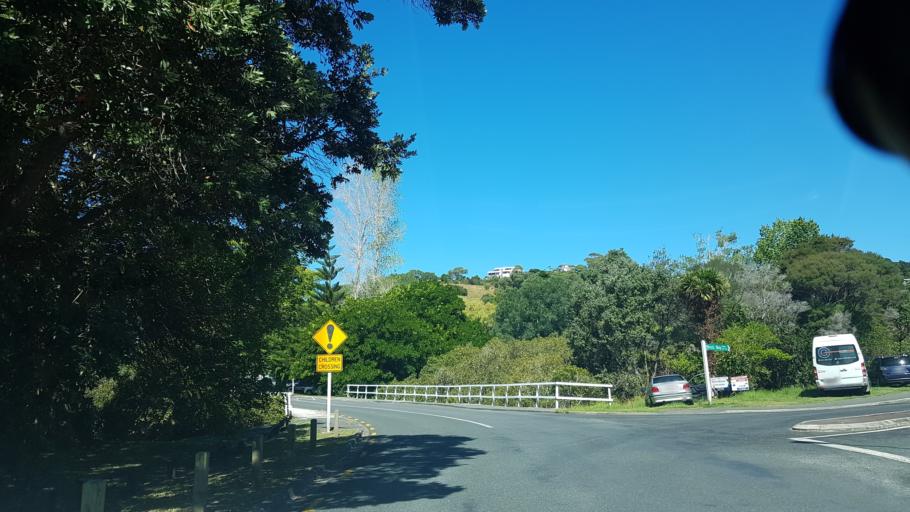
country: NZ
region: Auckland
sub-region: Auckland
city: Warkworth
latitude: -36.3927
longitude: 174.7262
